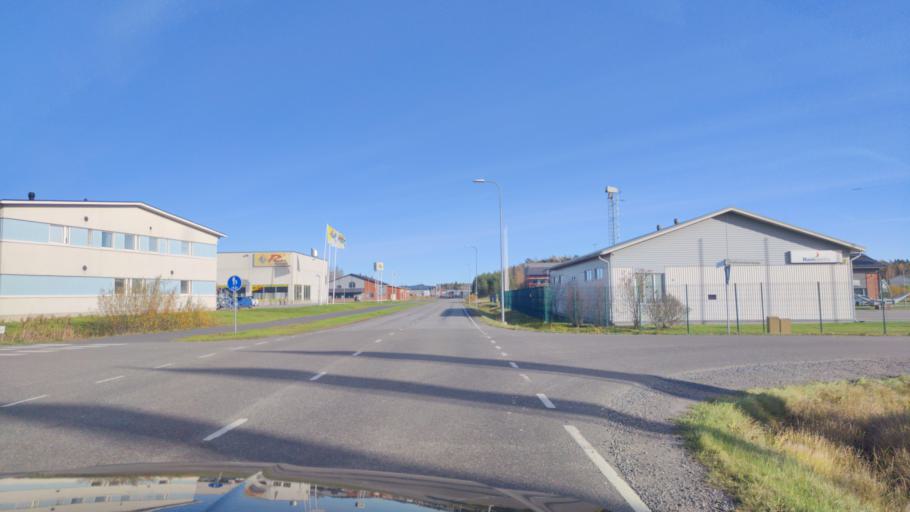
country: FI
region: Varsinais-Suomi
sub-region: Turku
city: Kaarina
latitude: 60.4199
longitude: 22.3840
